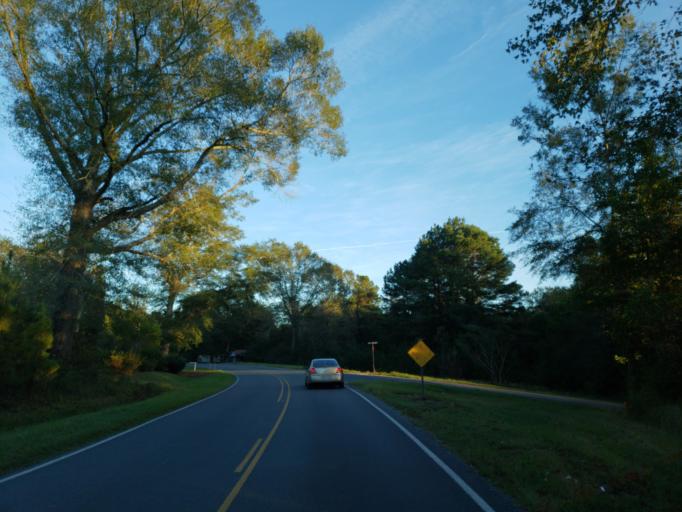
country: US
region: Mississippi
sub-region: Wayne County
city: Belmont
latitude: 31.4376
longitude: -88.4964
